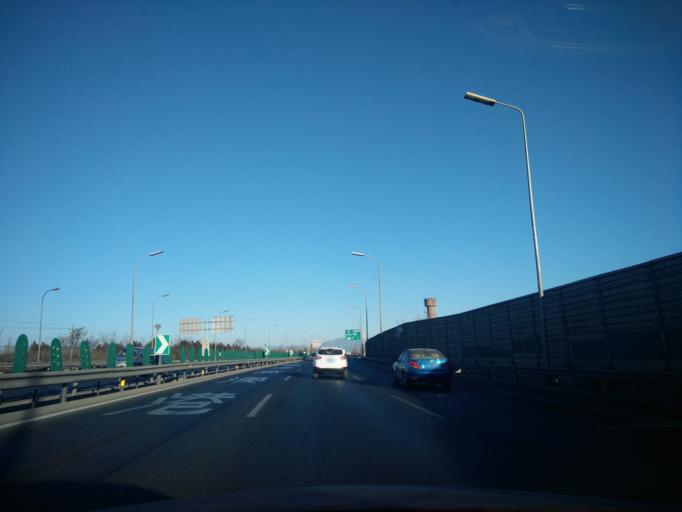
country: CN
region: Beijing
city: Fengtai
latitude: 39.8334
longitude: 116.2295
